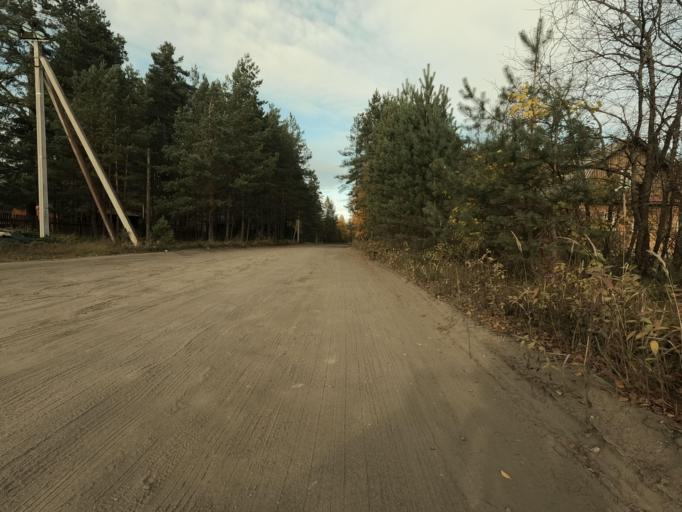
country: RU
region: Leningrad
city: Priladozhskiy
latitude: 59.6330
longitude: 31.3887
